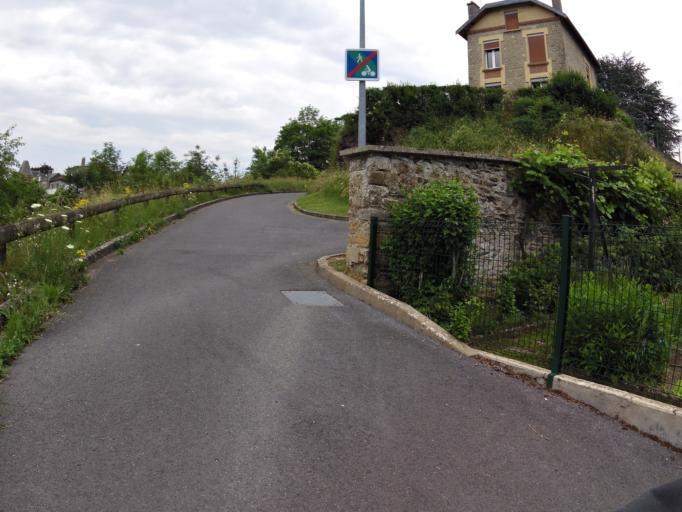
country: FR
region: Champagne-Ardenne
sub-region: Departement des Ardennes
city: Montcy-Notre-Dame
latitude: 49.7730
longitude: 4.7340
